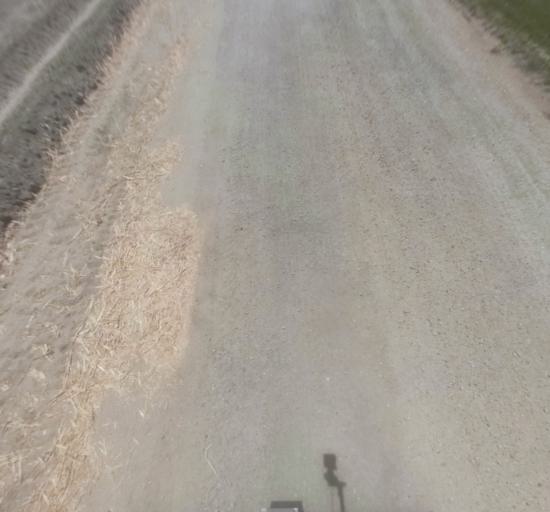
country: US
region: California
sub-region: Madera County
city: Chowchilla
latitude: 36.9971
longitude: -120.3465
